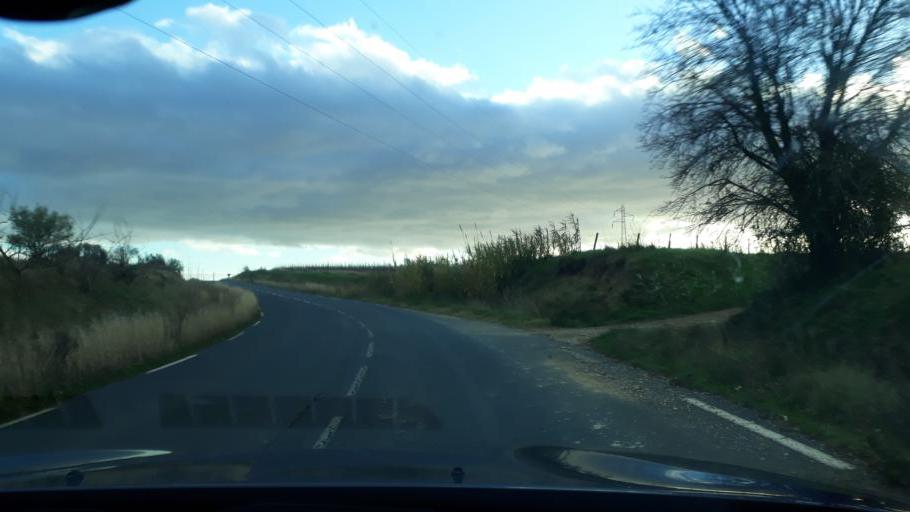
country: FR
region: Languedoc-Roussillon
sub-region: Departement de l'Herault
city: Nissan-lez-Enserune
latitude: 43.2975
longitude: 3.1312
